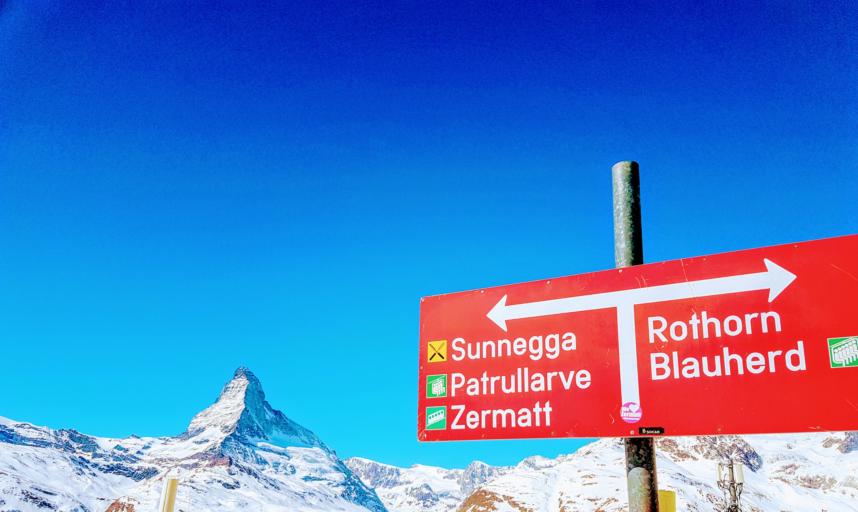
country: CH
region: Valais
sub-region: Visp District
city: Zermatt
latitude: 46.0172
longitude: 7.7706
